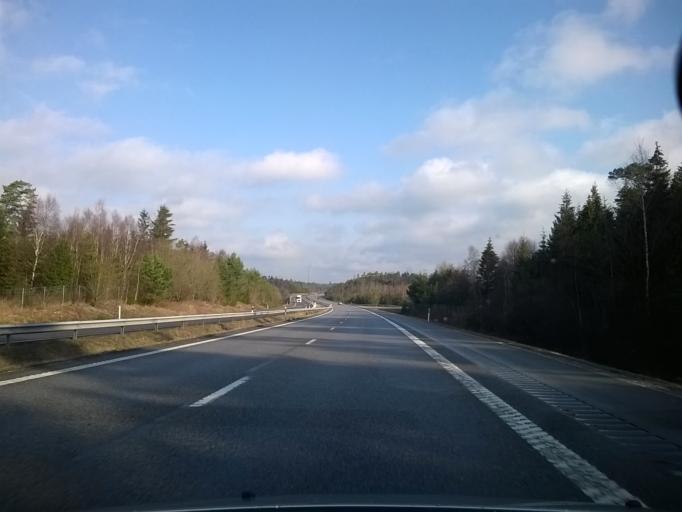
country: SE
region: Vaestra Goetaland
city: Svanesund
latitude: 58.1004
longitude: 11.8823
